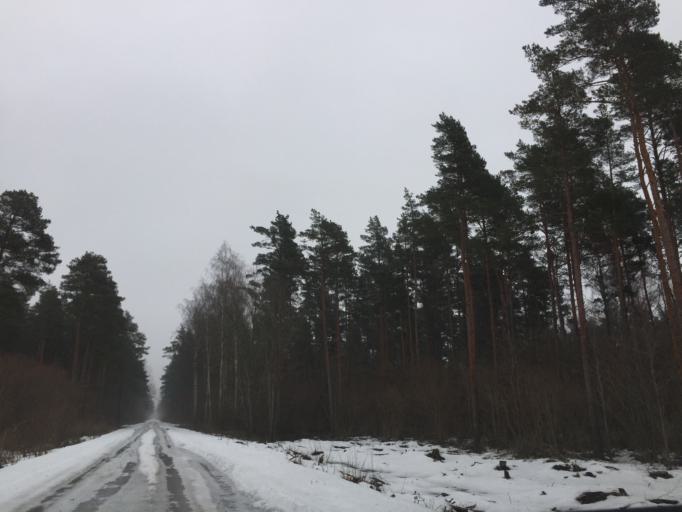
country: EE
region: Saare
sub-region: Kuressaare linn
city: Kuressaare
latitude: 58.2690
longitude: 22.5468
